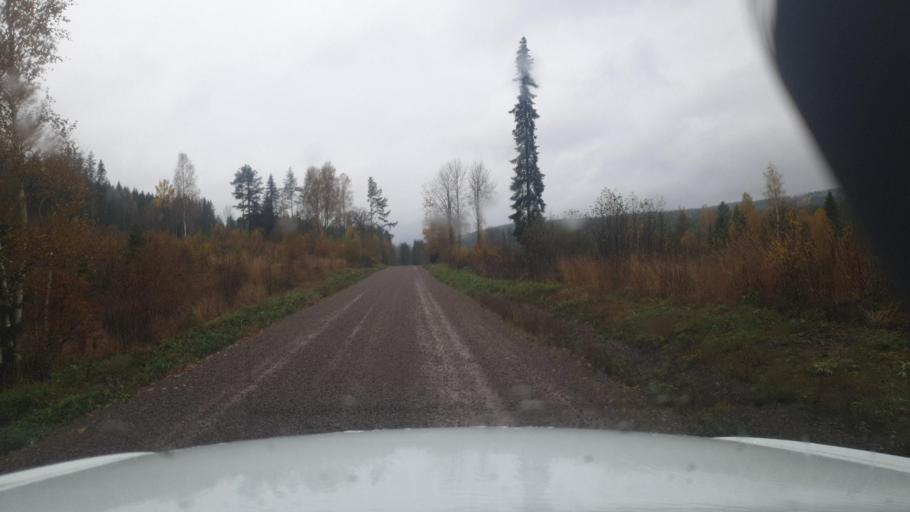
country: SE
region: Vaermland
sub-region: Eda Kommun
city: Charlottenberg
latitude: 60.0784
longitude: 12.5247
